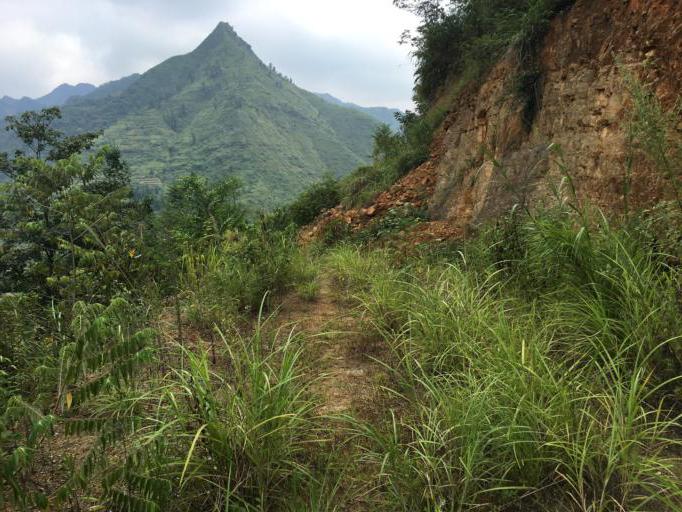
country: CN
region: Guangxi Zhuangzu Zizhiqu
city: Tongle
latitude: 25.3010
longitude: 106.1476
